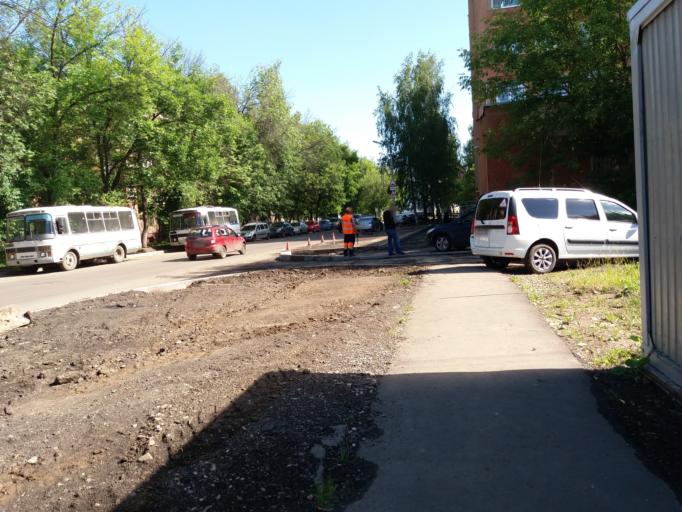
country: RU
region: Jaroslavl
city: Yaroslavl
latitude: 57.6393
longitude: 39.8517
